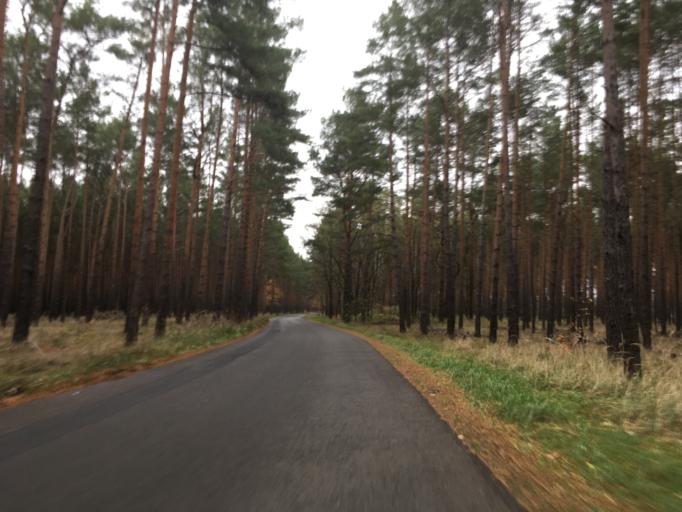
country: DE
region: Brandenburg
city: Mullrose
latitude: 52.2642
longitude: 14.4773
